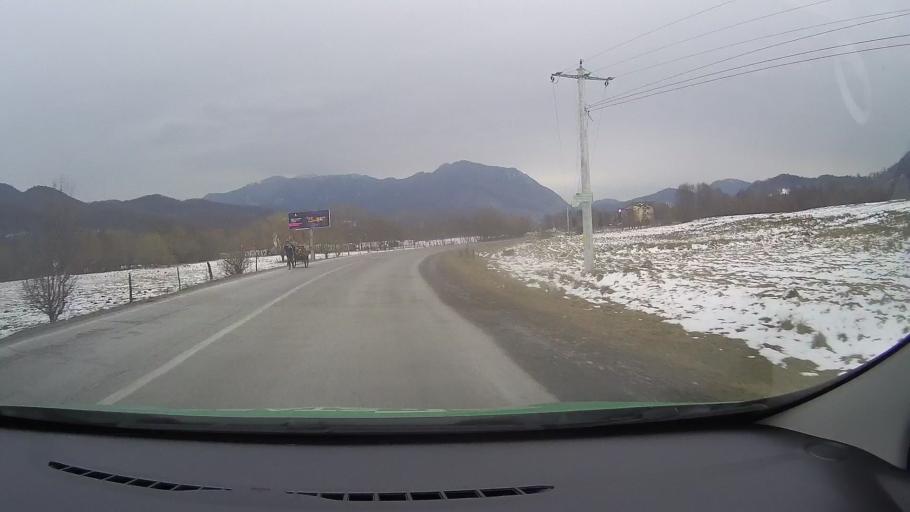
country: RO
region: Brasov
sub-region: Oras Rasnov
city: Rasnov
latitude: 45.5560
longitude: 25.4767
